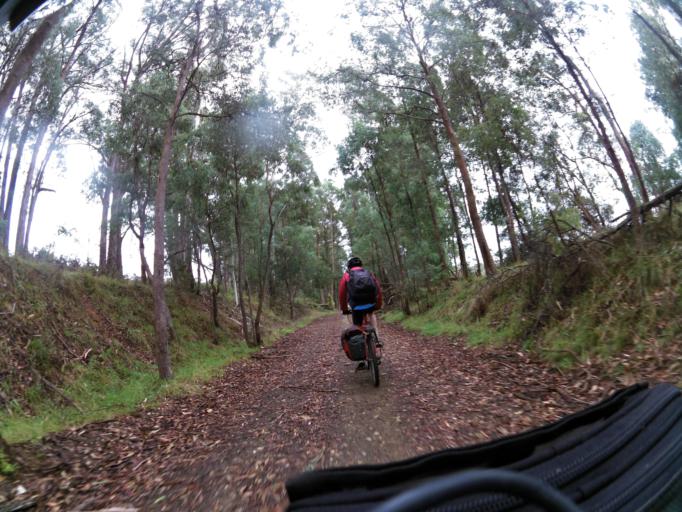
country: AU
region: New South Wales
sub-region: Greater Hume Shire
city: Holbrook
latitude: -36.1595
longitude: 147.4863
